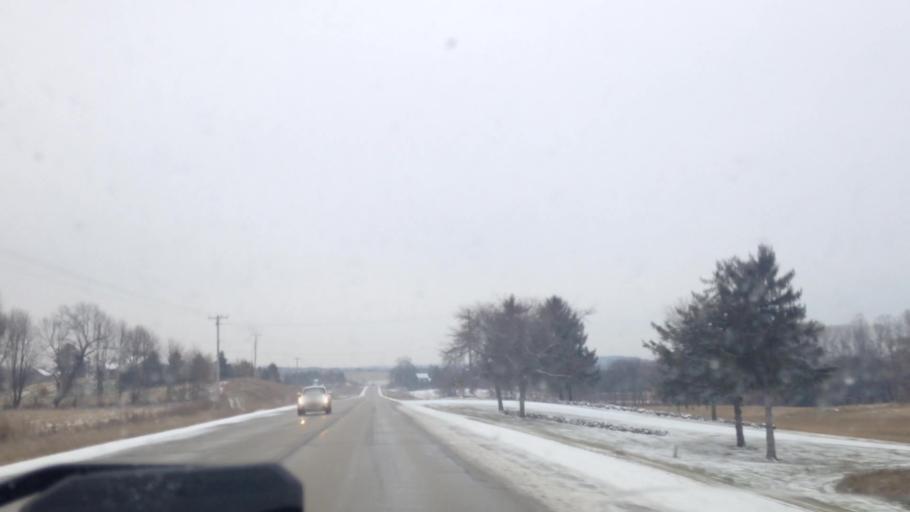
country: US
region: Wisconsin
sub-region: Dodge County
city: Hustisford
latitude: 43.2496
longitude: -88.5179
